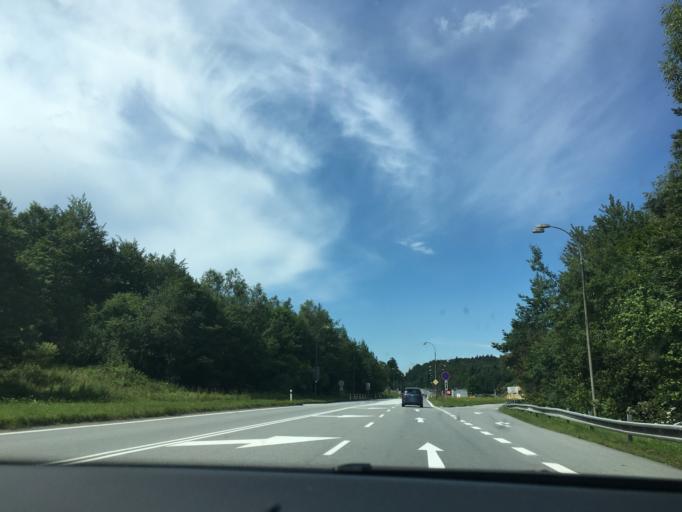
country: PL
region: Subcarpathian Voivodeship
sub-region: Powiat krosnienski
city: Jasliska
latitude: 49.4097
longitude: 21.7009
